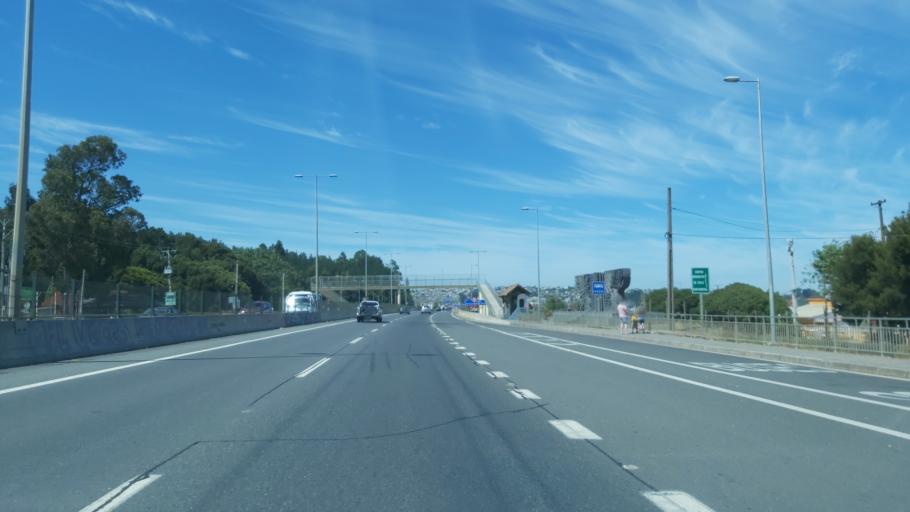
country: CL
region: Biobio
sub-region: Provincia de Concepcion
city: Coronel
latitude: -37.0620
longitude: -73.1411
